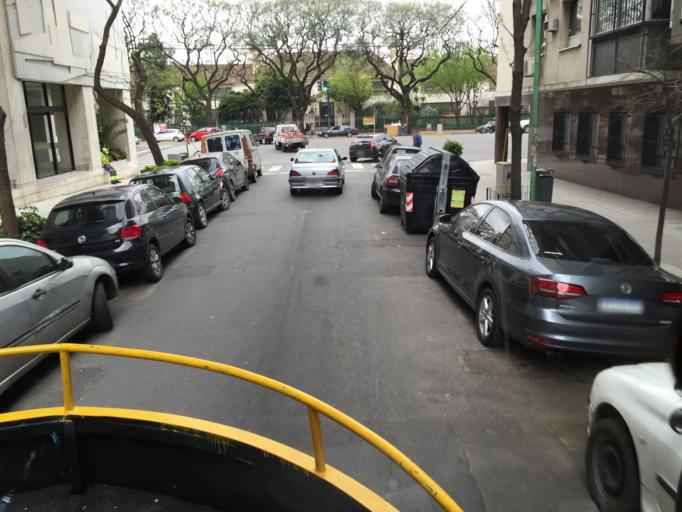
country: AR
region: Buenos Aires F.D.
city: Colegiales
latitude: -34.5647
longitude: -58.4359
